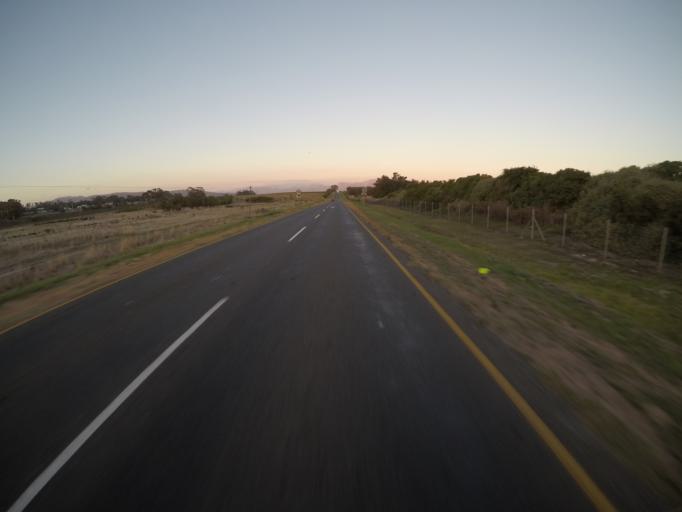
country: ZA
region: Western Cape
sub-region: Cape Winelands District Municipality
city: Paarl
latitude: -33.8065
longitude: 18.8789
